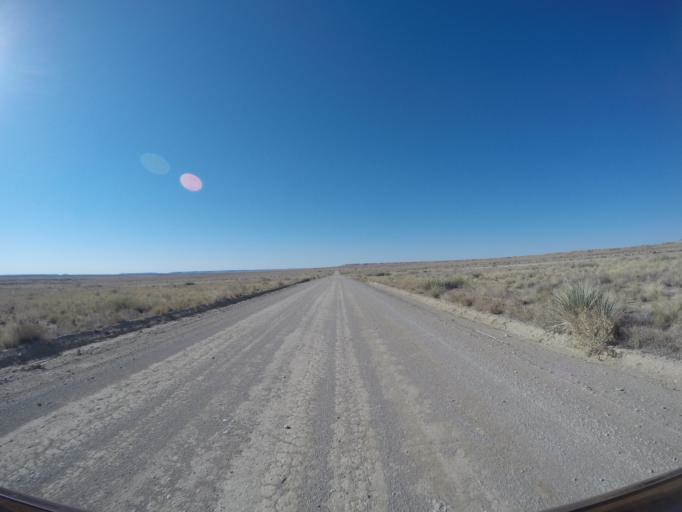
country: US
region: Colorado
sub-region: Otero County
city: La Junta
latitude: 37.7844
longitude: -103.5348
